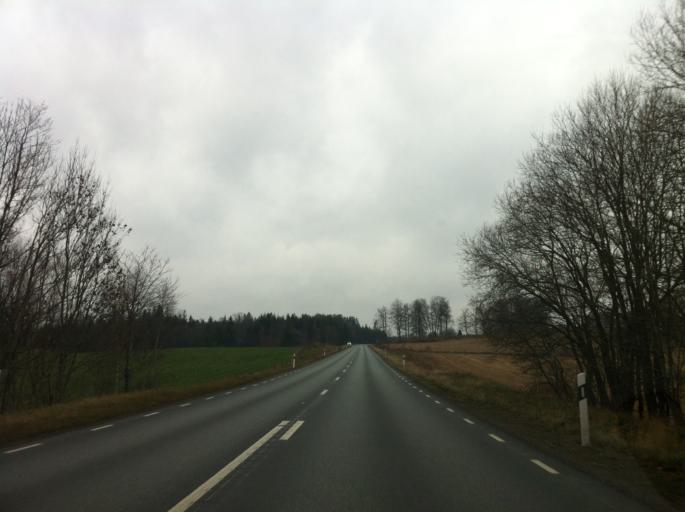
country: SE
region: Joenkoeping
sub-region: Vetlanda Kommun
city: Landsbro
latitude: 57.3915
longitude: 14.8074
